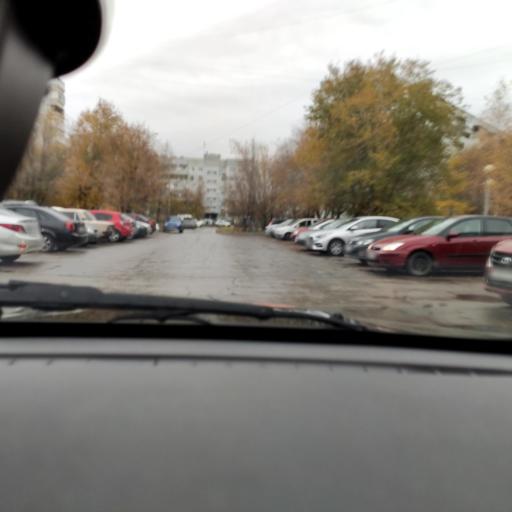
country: RU
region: Samara
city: Tol'yatti
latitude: 53.5463
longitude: 49.3393
